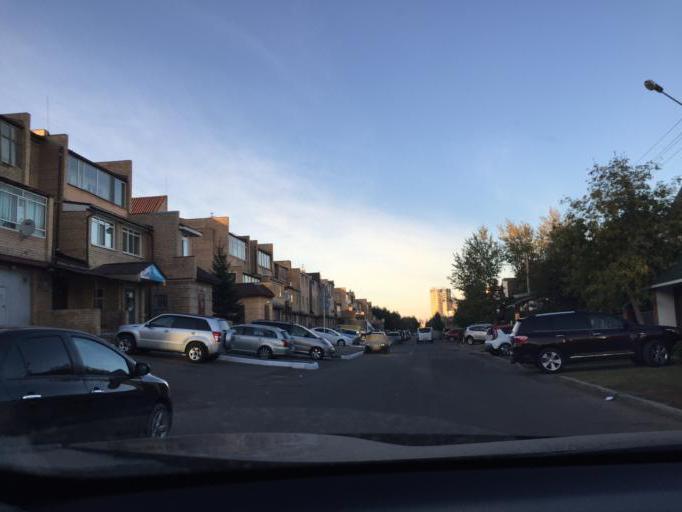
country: KZ
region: Astana Qalasy
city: Astana
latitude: 51.1380
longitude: 71.4177
